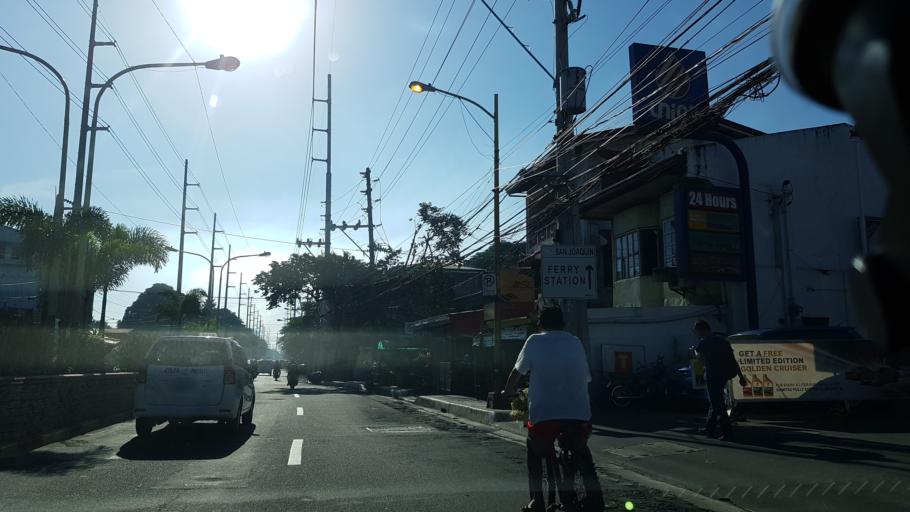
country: PH
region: Calabarzon
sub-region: Province of Rizal
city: Pateros
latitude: 14.5544
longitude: 121.0664
